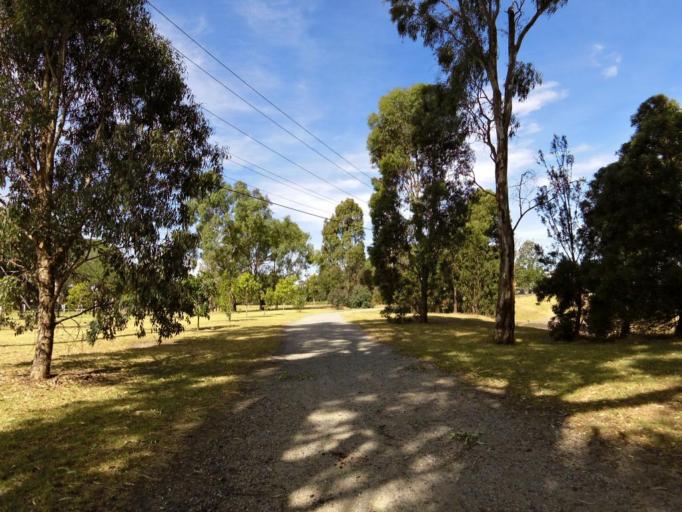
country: AU
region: Victoria
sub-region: Casey
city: Doveton
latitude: -37.9994
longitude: 145.2357
